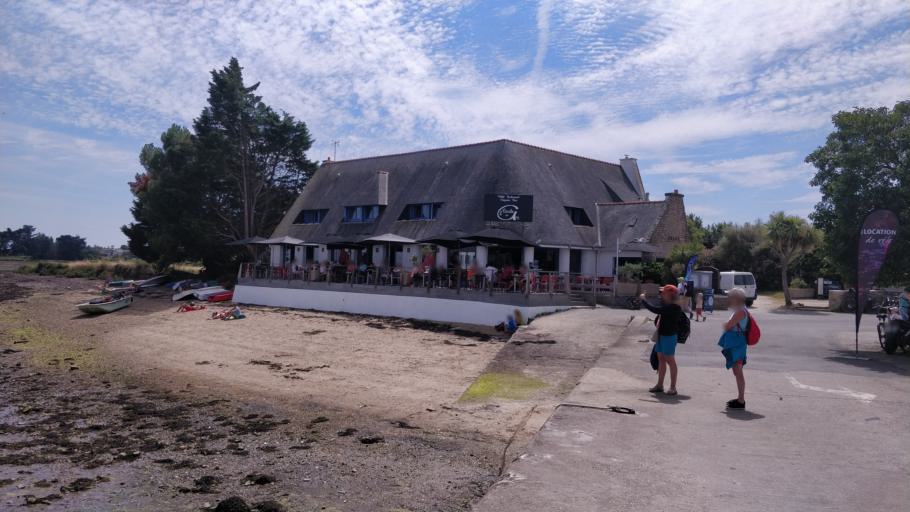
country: FR
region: Brittany
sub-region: Departement du Morbihan
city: Arradon
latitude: 47.6058
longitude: -2.7930
